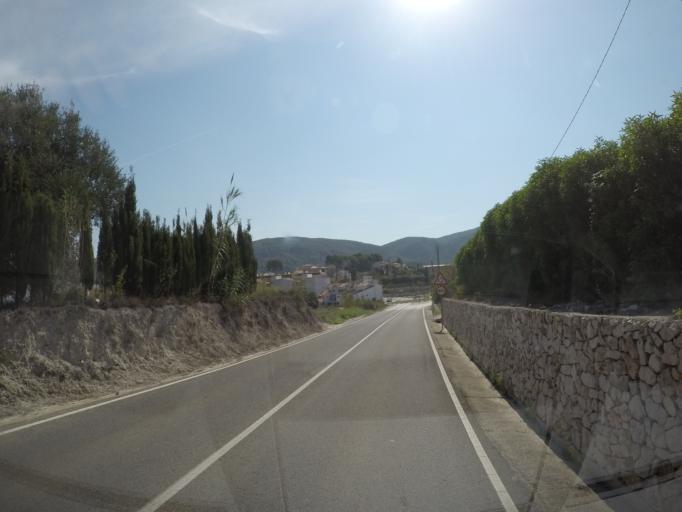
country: ES
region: Valencia
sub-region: Provincia de Alicante
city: Orba
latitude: 38.7796
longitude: -0.0679
